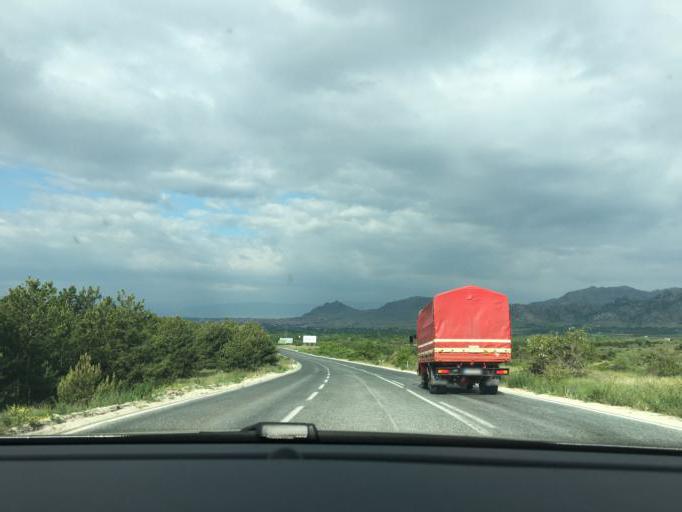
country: MK
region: Prilep
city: Prilep
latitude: 41.3704
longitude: 21.6222
